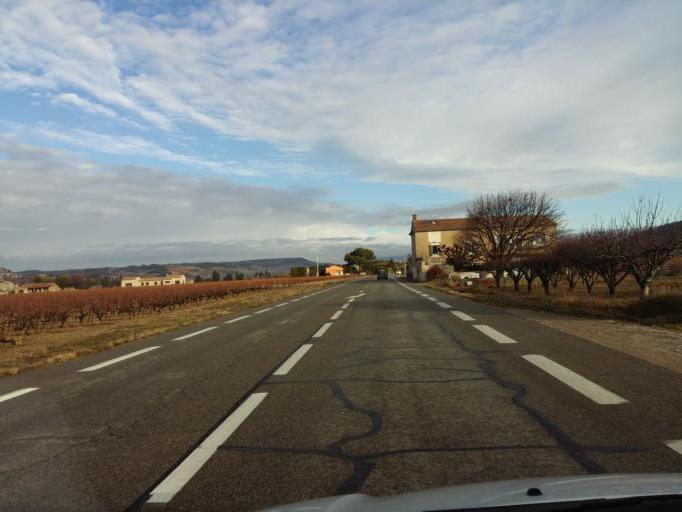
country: FR
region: Provence-Alpes-Cote d'Azur
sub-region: Departement du Vaucluse
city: Sablet
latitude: 44.2069
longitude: 5.0013
